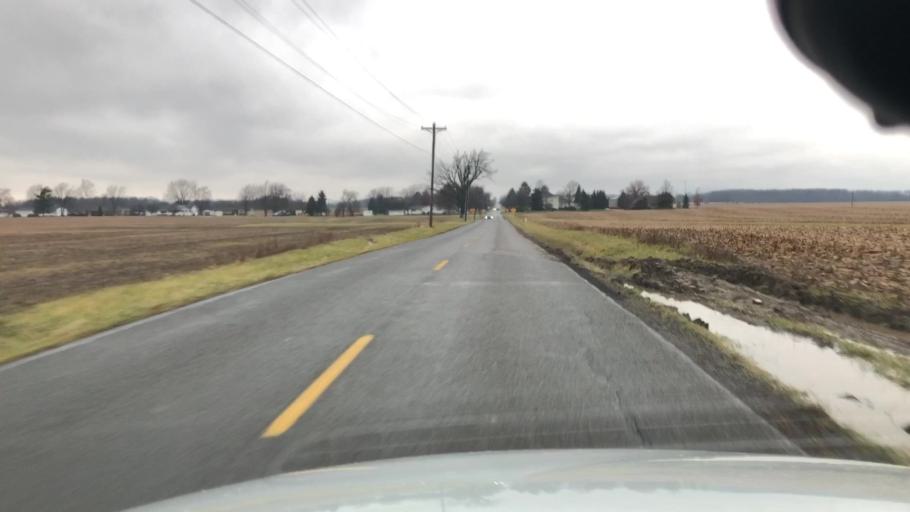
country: US
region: Ohio
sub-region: Allen County
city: Lima
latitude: 40.7859
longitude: -84.0131
